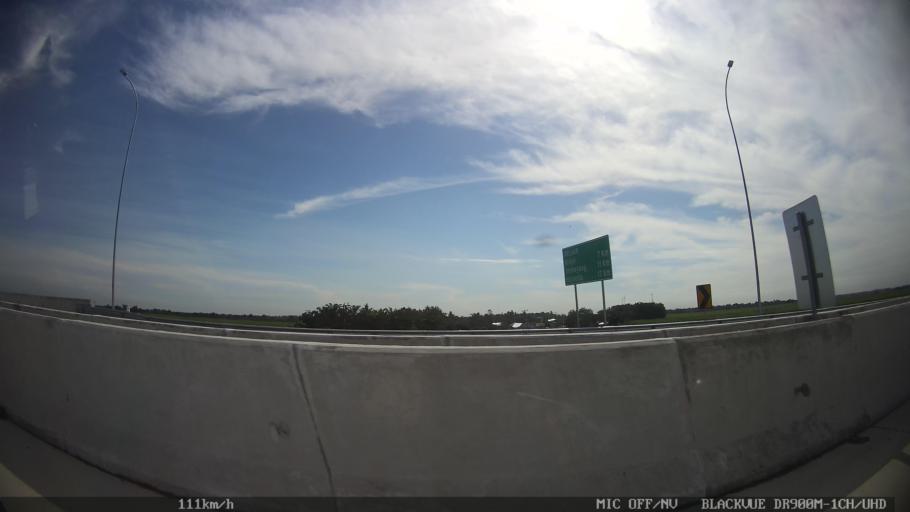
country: ID
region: North Sumatra
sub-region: Kabupaten Langkat
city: Stabat
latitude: 3.6997
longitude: 98.5400
